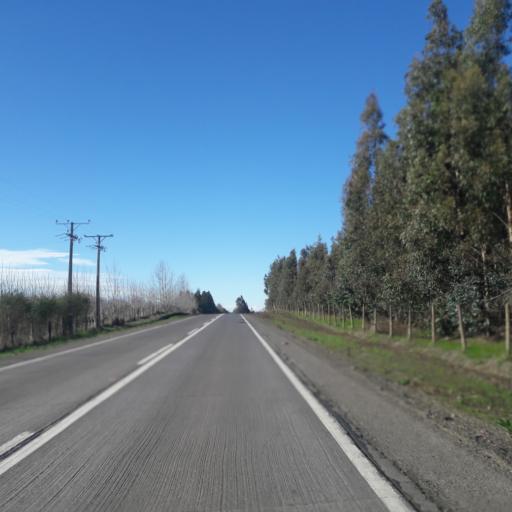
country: CL
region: Araucania
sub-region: Provincia de Malleco
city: Angol
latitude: -37.7528
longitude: -72.5841
